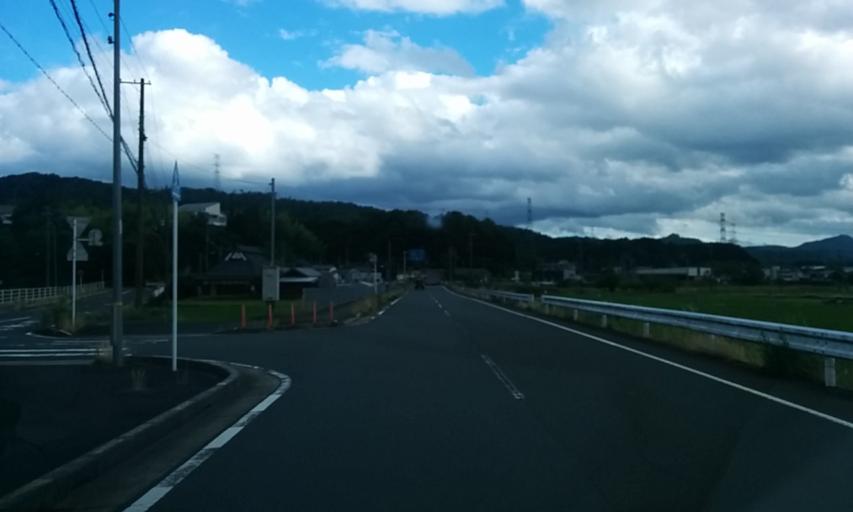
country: JP
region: Kyoto
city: Ayabe
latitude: 35.3296
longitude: 135.2930
